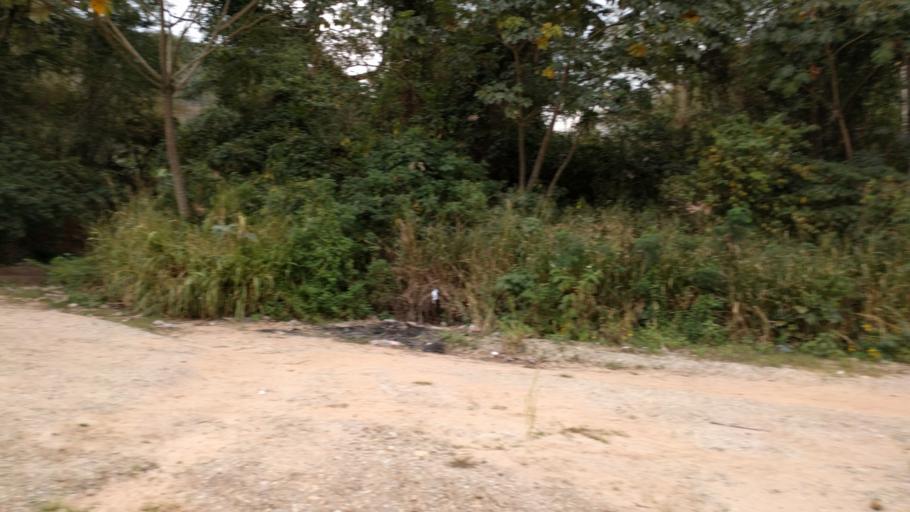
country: BO
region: Santa Cruz
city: Jorochito
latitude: -18.1684
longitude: -63.5263
